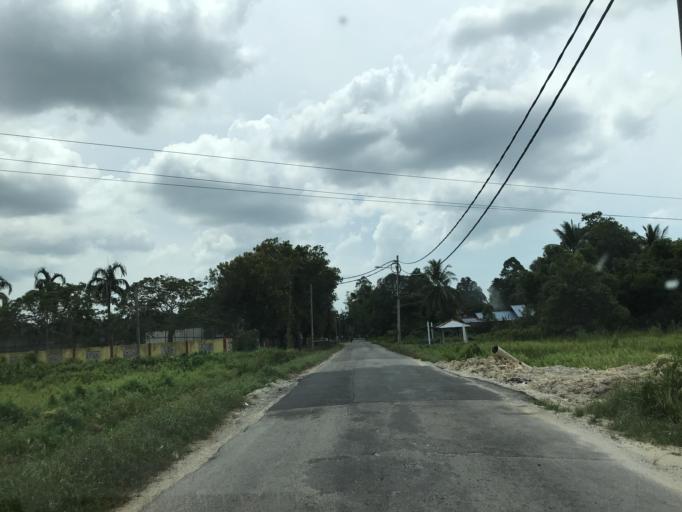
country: MY
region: Kelantan
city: Tumpat
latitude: 6.1491
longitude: 102.1878
